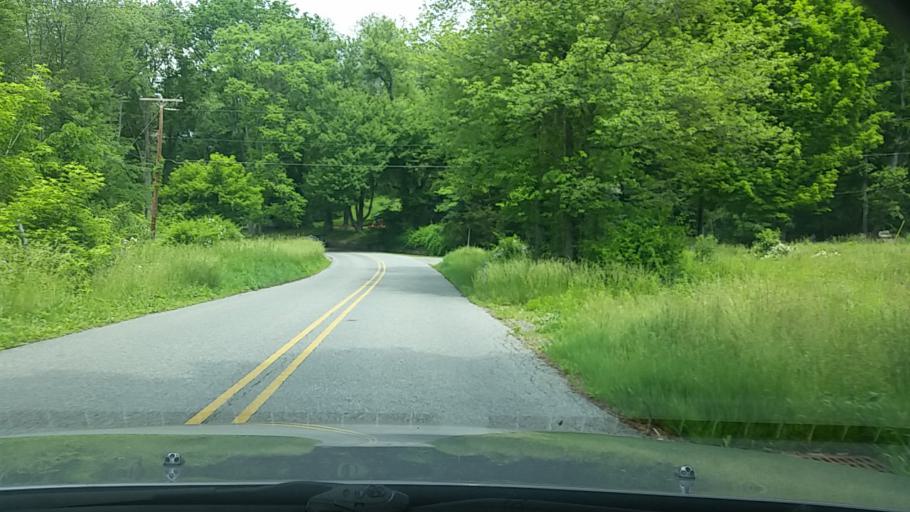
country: US
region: New Jersey
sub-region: Warren County
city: Oxford
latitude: 40.8518
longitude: -74.9814
